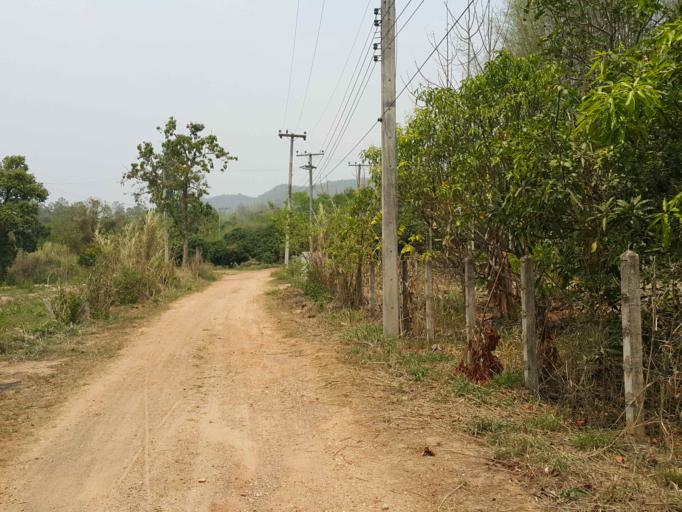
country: TH
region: Chiang Mai
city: San Sai
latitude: 18.9308
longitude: 99.0308
